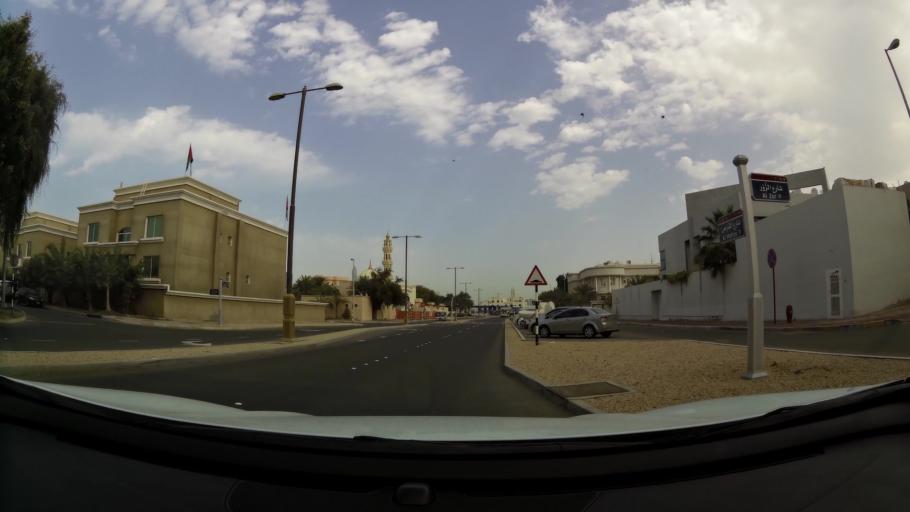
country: AE
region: Abu Dhabi
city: Abu Dhabi
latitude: 24.4557
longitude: 54.3476
